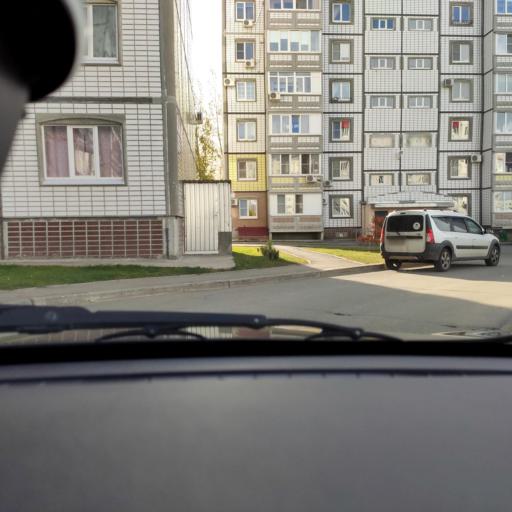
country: RU
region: Samara
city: Tol'yatti
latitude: 53.5239
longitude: 49.3347
